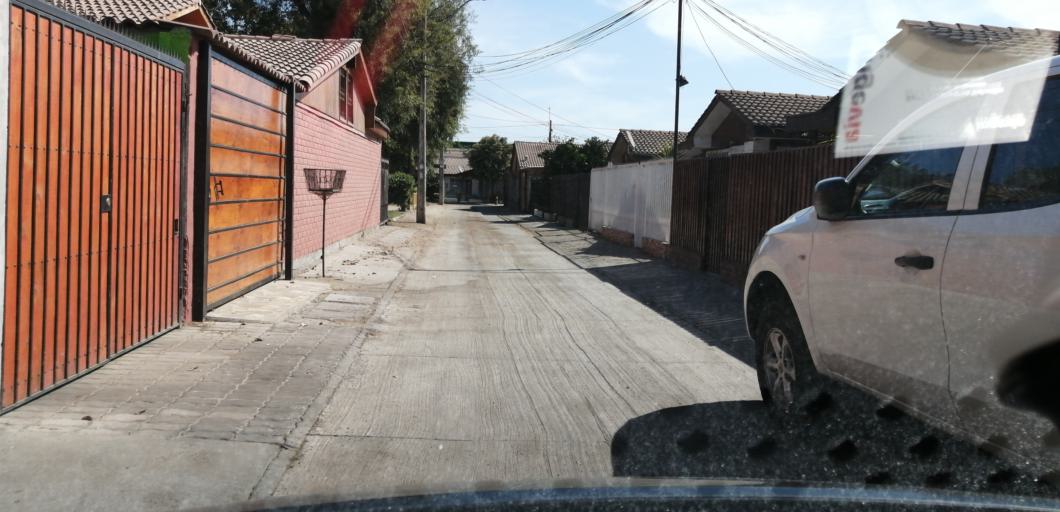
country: CL
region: Santiago Metropolitan
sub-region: Provincia de Santiago
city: Lo Prado
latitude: -33.4662
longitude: -70.7352
